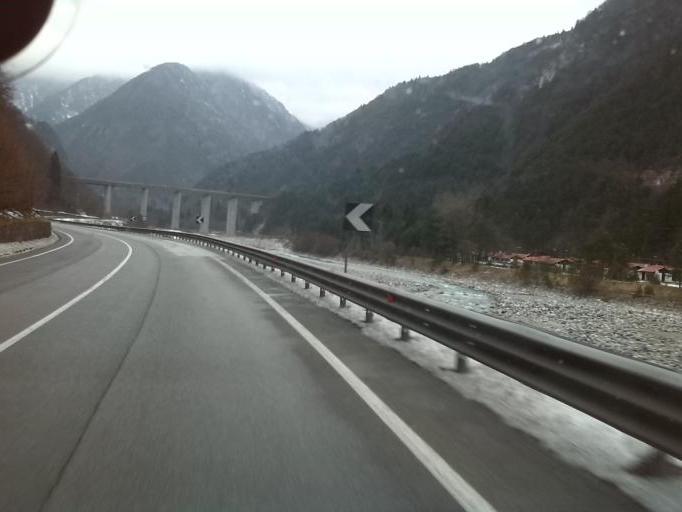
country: IT
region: Friuli Venezia Giulia
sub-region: Provincia di Udine
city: Dogna
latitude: 46.4531
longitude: 13.3116
